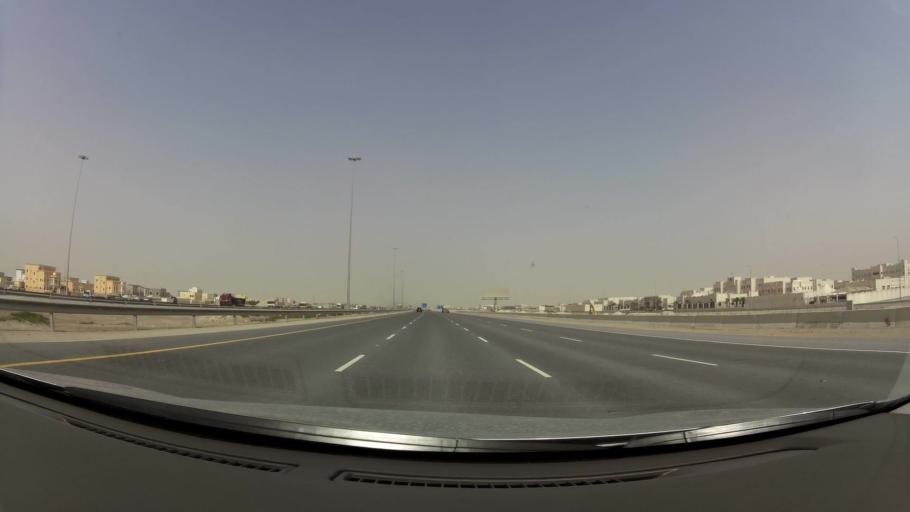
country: QA
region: Baladiyat ar Rayyan
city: Ar Rayyan
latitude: 25.1863
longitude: 51.3638
